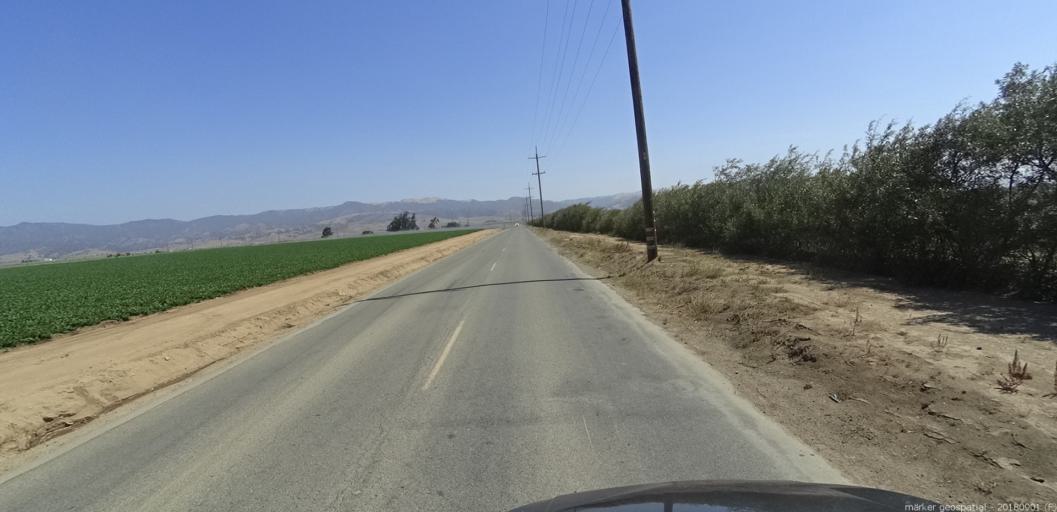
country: US
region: California
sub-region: Monterey County
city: Chualar
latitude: 36.5792
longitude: -121.5040
